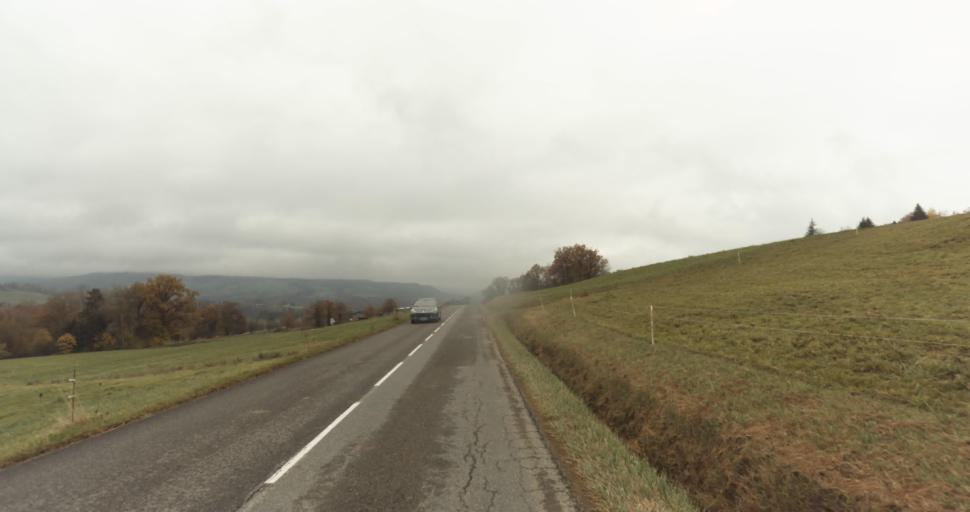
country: FR
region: Rhone-Alpes
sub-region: Departement de la Haute-Savoie
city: Evires
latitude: 46.0246
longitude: 6.2021
